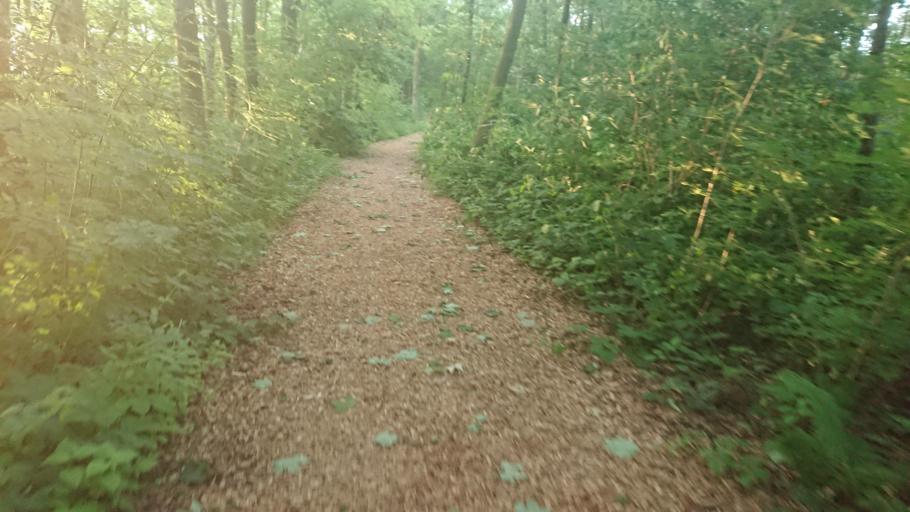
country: GB
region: England
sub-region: Lancashire
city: Galgate
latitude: 54.0048
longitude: -2.7832
